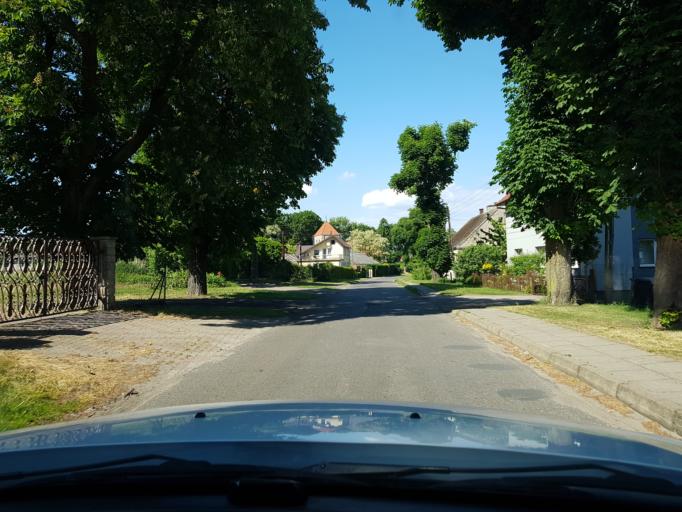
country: PL
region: West Pomeranian Voivodeship
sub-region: Powiat gryfinski
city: Gryfino
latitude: 53.1738
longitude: 14.5417
